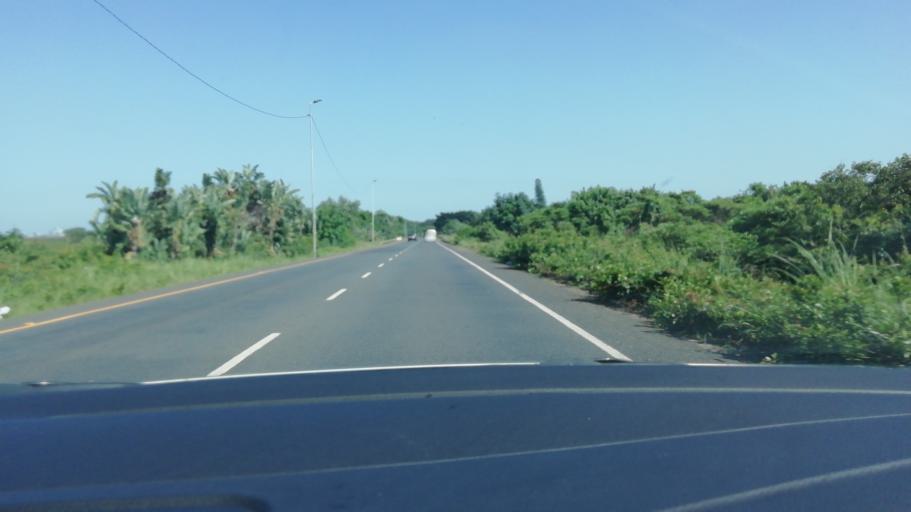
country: ZA
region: KwaZulu-Natal
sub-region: uThungulu District Municipality
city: Richards Bay
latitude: -28.7755
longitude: 32.0734
